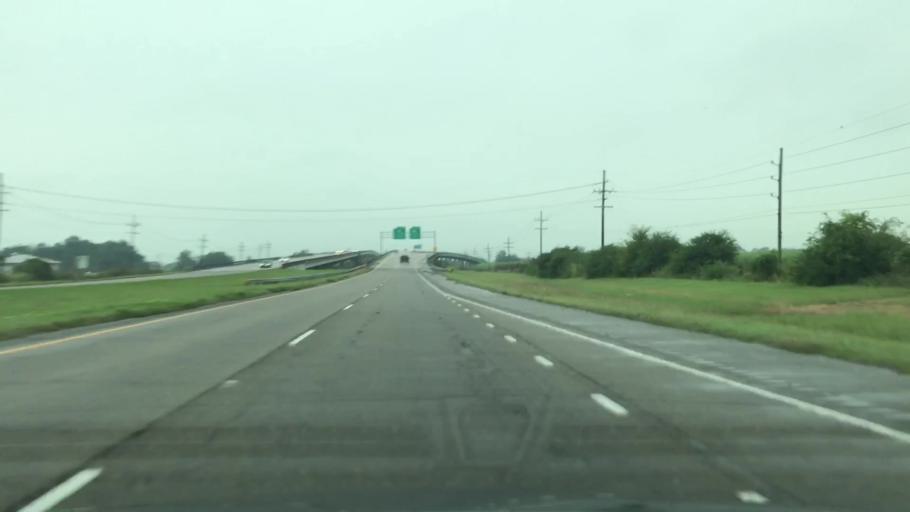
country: US
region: Louisiana
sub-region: Lafourche Parish
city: Mathews
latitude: 29.7139
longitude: -90.5668
